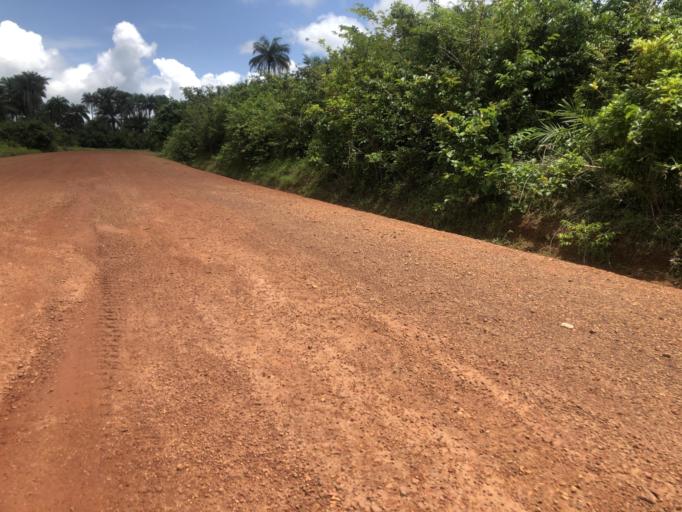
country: SL
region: Northern Province
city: Port Loko
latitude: 8.7149
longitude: -12.8340
